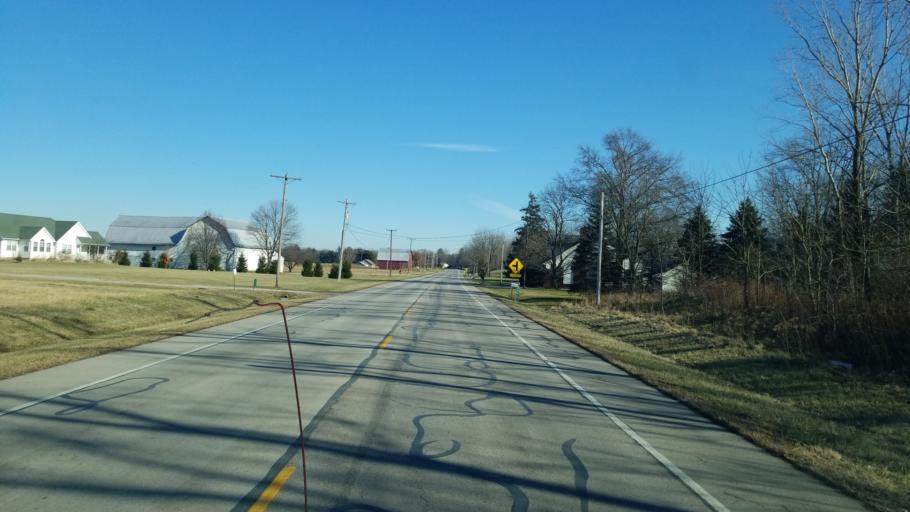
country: US
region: Ohio
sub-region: Lucas County
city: Whitehouse
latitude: 41.4660
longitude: -83.7709
